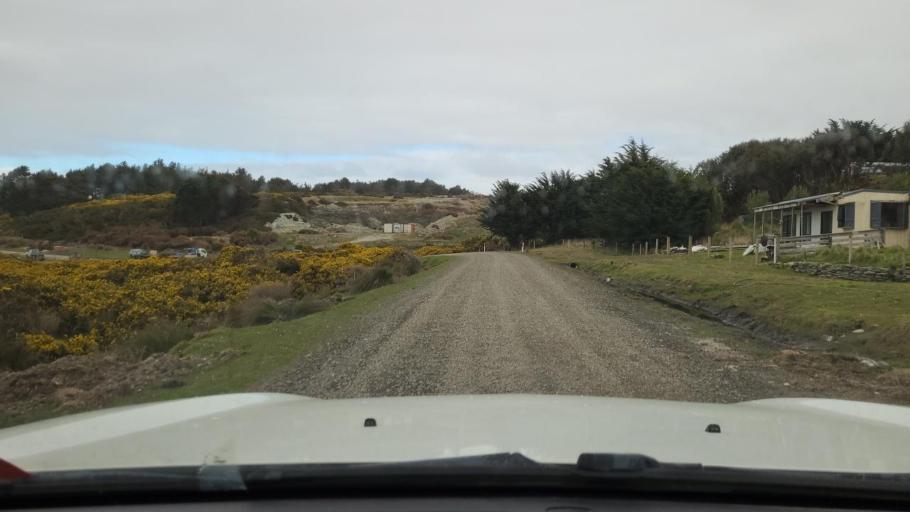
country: NZ
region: Chatham Islands
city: Waitangi
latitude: -43.8104
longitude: -176.7112
